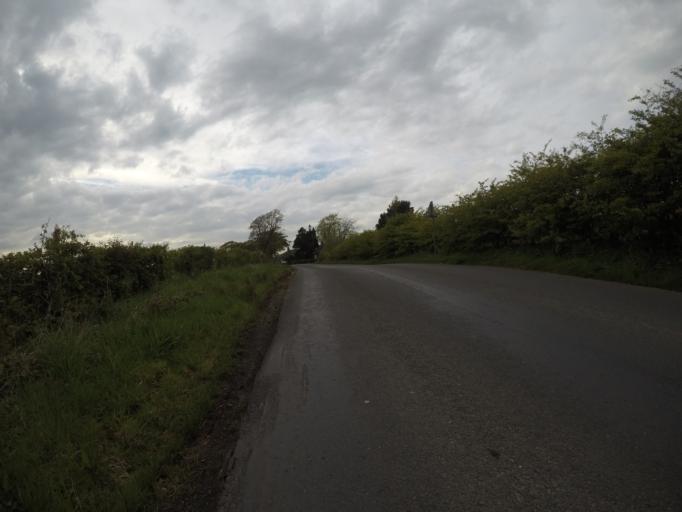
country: GB
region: Scotland
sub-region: East Ayrshire
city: Kilmarnock
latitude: 55.6452
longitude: -4.4838
